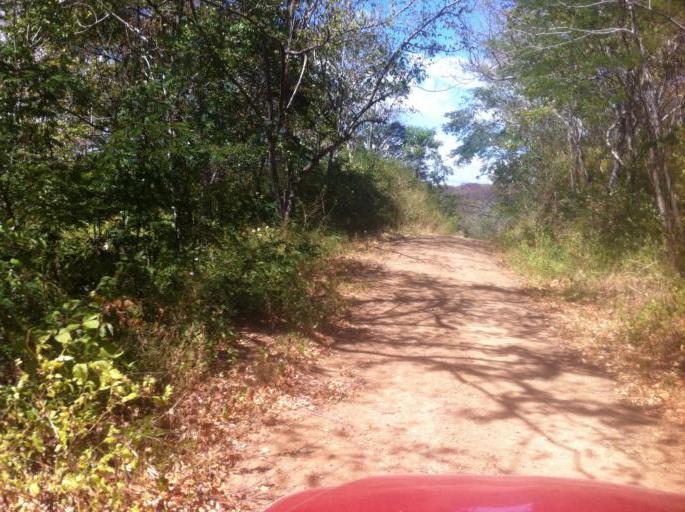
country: NI
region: Rivas
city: San Juan del Sur
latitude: 11.3234
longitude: -85.9449
